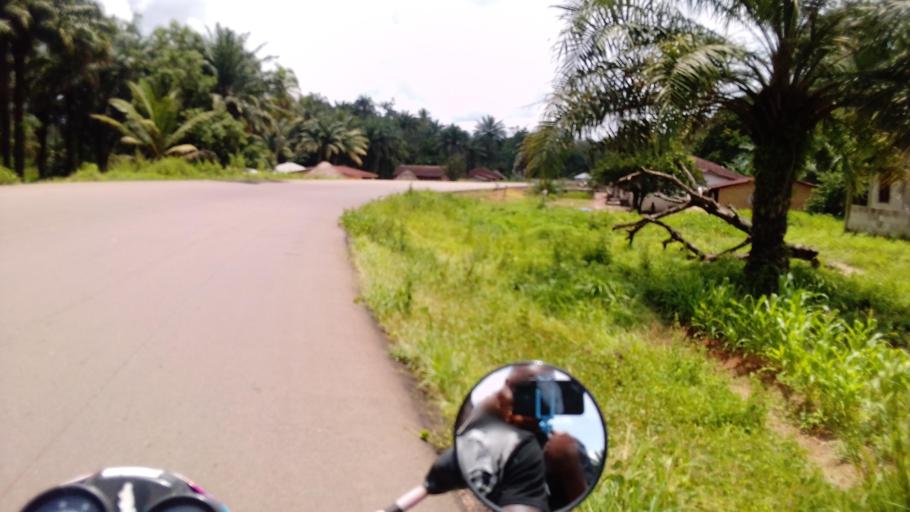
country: SL
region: Northern Province
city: Makeni
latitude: 9.0928
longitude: -12.1937
